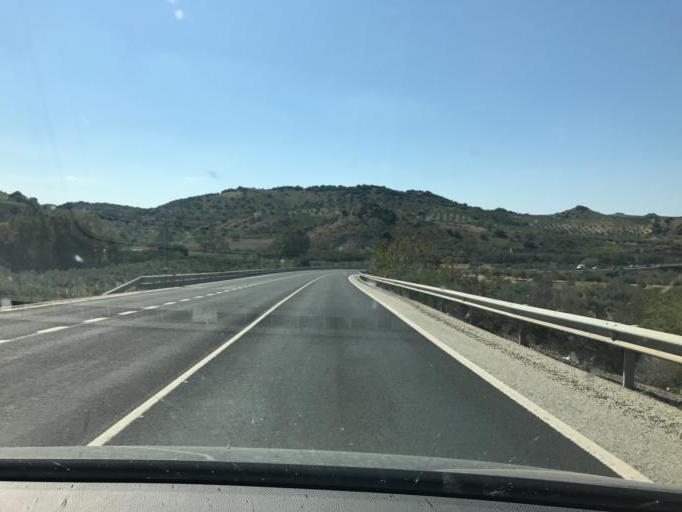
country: ES
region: Andalusia
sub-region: Province of Cordoba
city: Fuente-Tojar
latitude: 37.5758
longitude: -4.1553
